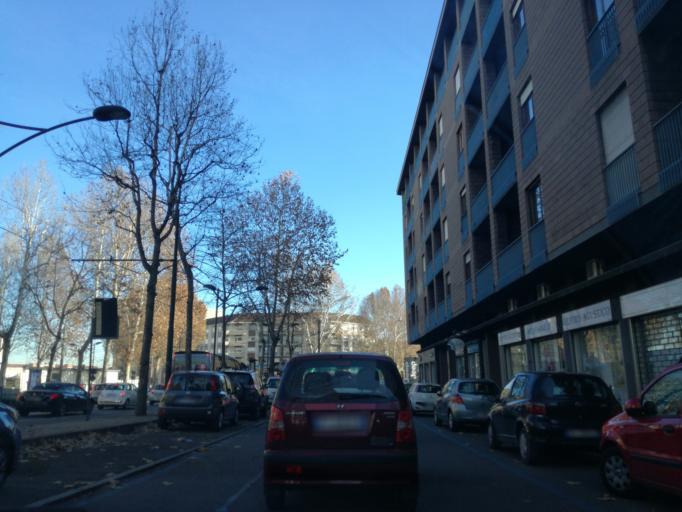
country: IT
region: Piedmont
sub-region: Provincia di Torino
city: Turin
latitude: 45.0786
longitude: 7.6749
